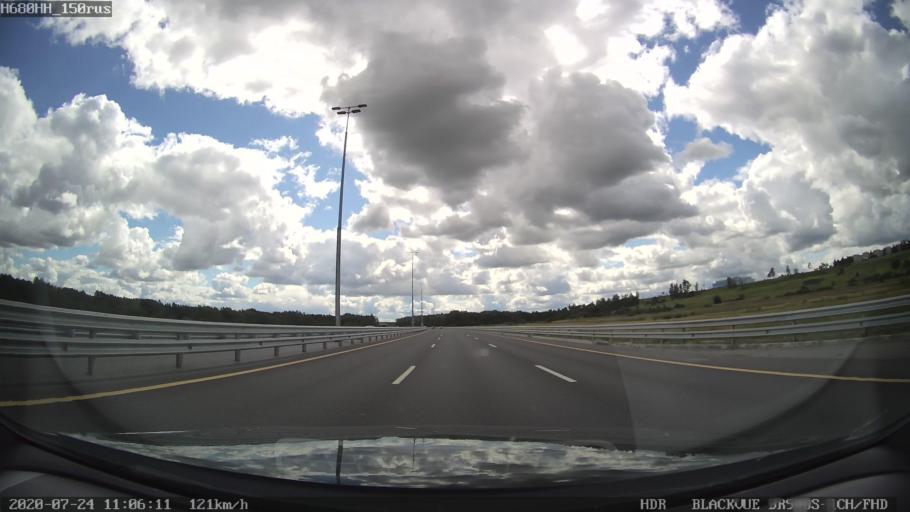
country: RU
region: St.-Petersburg
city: Shushary
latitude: 59.7667
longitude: 30.3689
